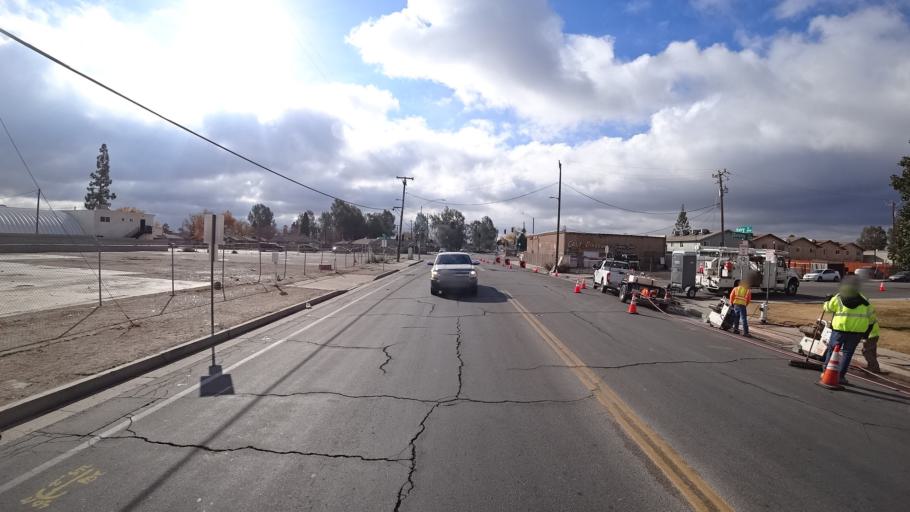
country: US
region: California
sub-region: Kern County
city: Bakersfield
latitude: 35.3693
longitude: -118.9838
